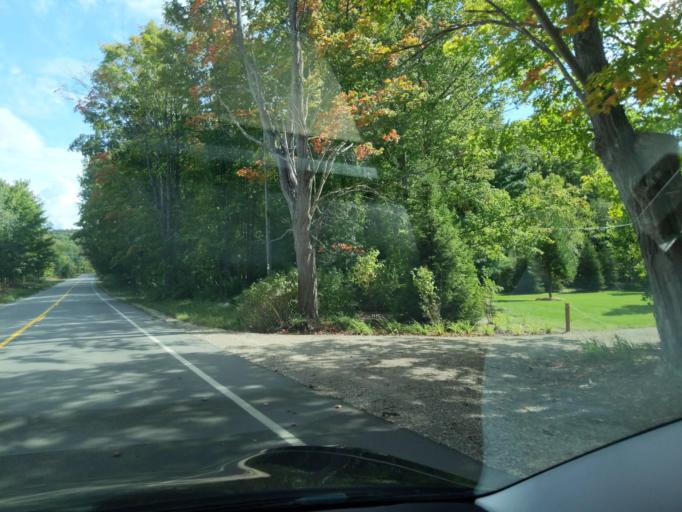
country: US
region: Michigan
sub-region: Antrim County
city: Bellaire
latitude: 45.0411
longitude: -85.3019
